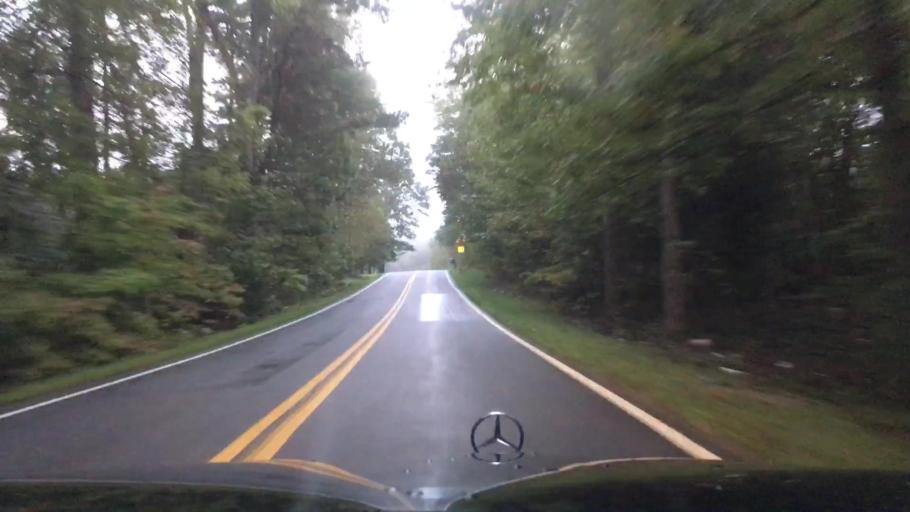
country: US
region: Virginia
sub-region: Campbell County
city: Timberlake
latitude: 37.2509
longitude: -79.2796
